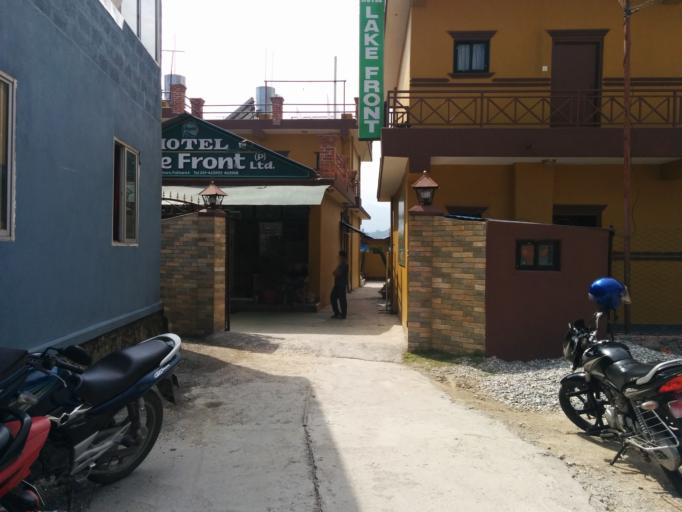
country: NP
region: Western Region
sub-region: Gandaki Zone
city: Pokhara
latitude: 28.2177
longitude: 83.9583
